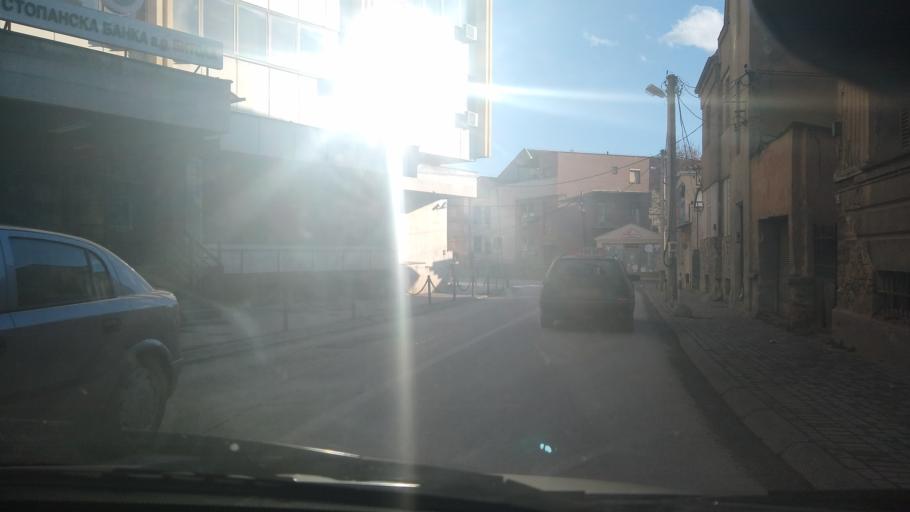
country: MK
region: Bitola
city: Bitola
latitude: 41.0301
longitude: 21.3361
